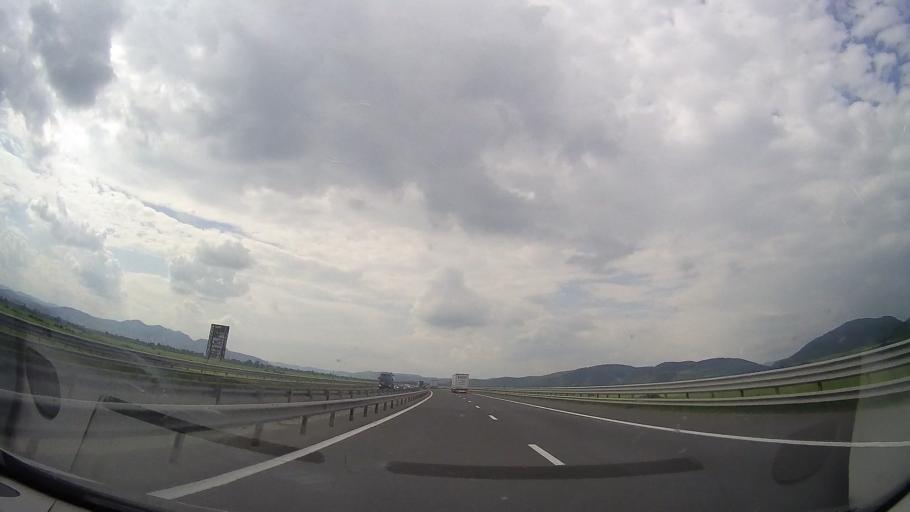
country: RO
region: Hunedoara
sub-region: Oras Simeria
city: Simeria
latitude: 45.8686
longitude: 23.0200
